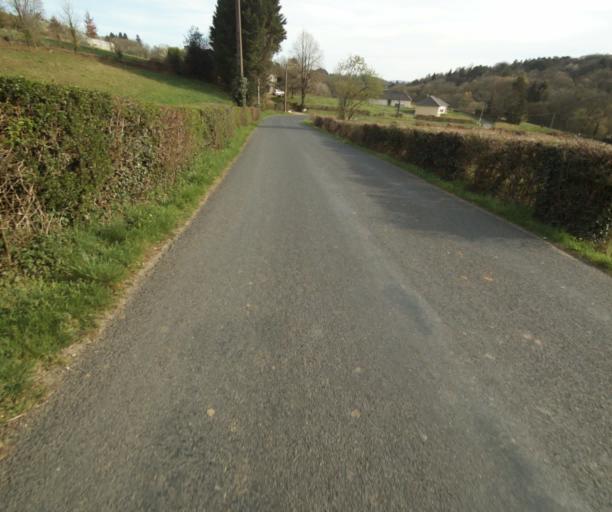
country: FR
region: Limousin
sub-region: Departement de la Correze
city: Naves
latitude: 45.3162
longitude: 1.7581
